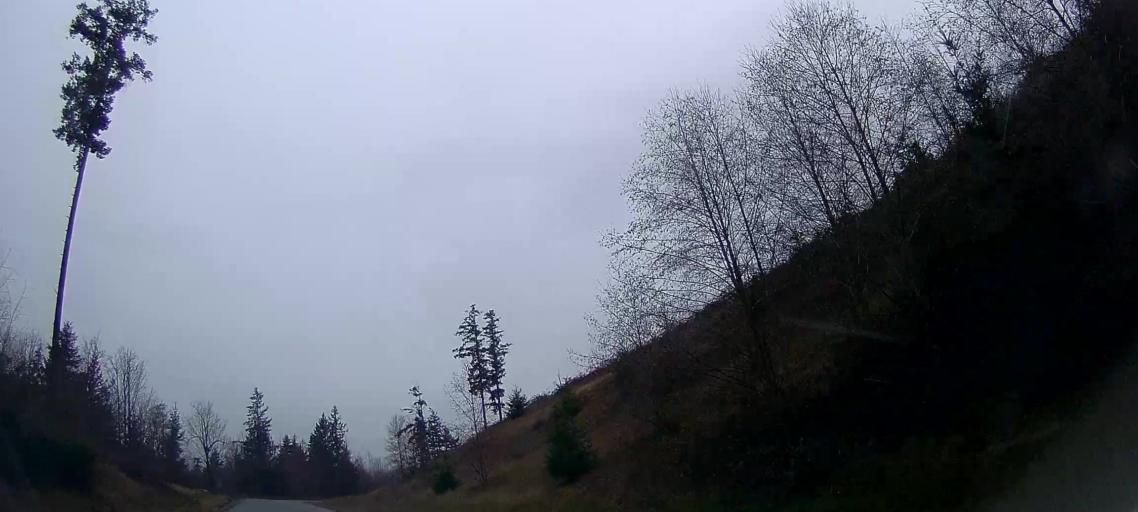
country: US
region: Washington
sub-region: Skagit County
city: Mount Vernon
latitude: 48.3695
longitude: -122.3075
